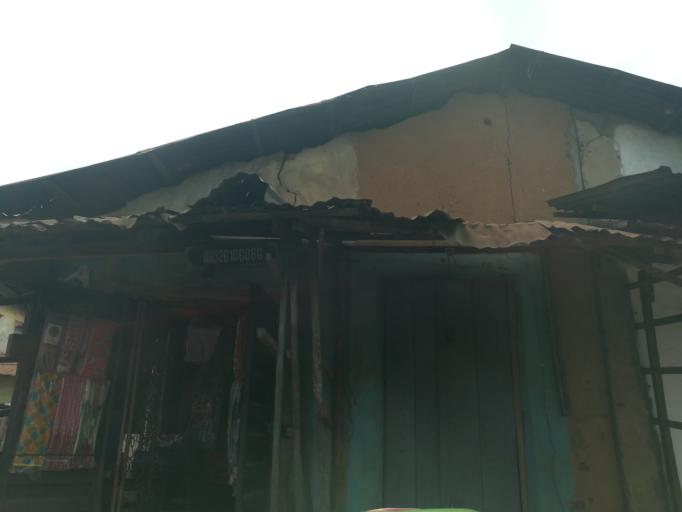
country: NG
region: Lagos
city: Ikorodu
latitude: 6.6133
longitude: 3.5088
